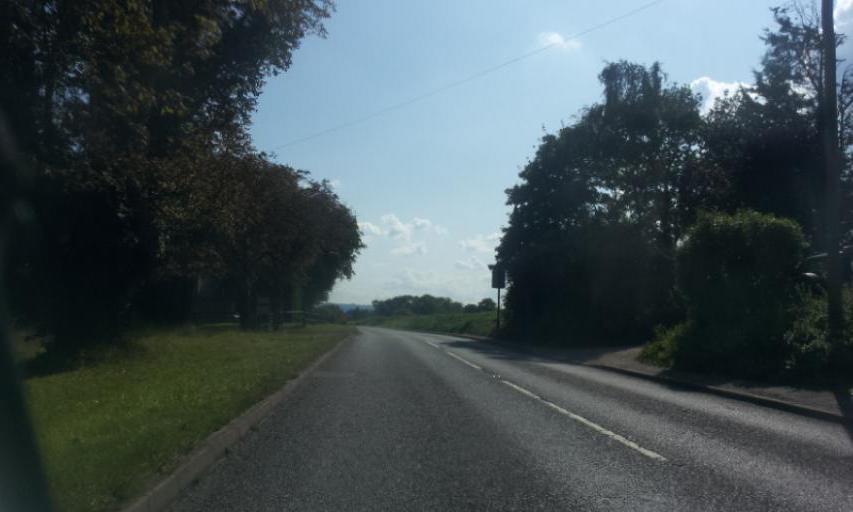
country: GB
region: England
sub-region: Kent
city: Wateringbury
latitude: 51.2428
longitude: 0.4110
